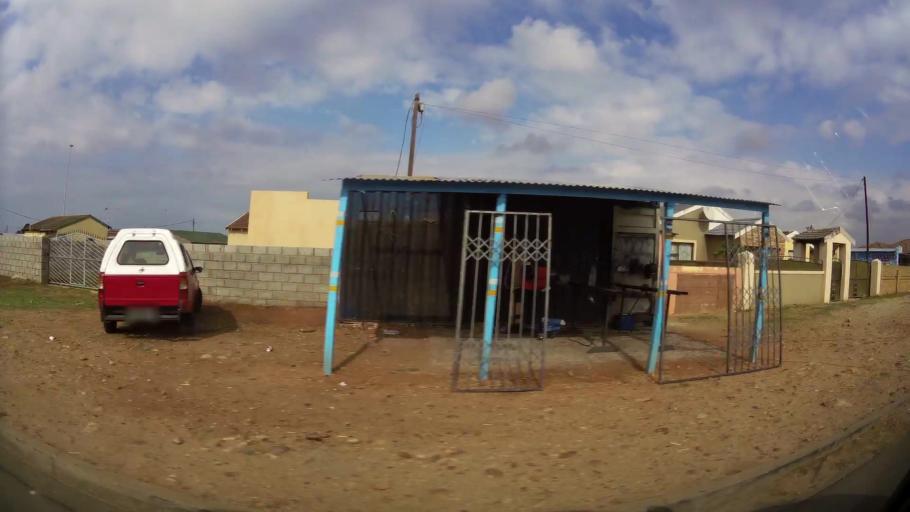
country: ZA
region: Eastern Cape
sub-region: Nelson Mandela Bay Metropolitan Municipality
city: Port Elizabeth
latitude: -33.8158
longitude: 25.5855
